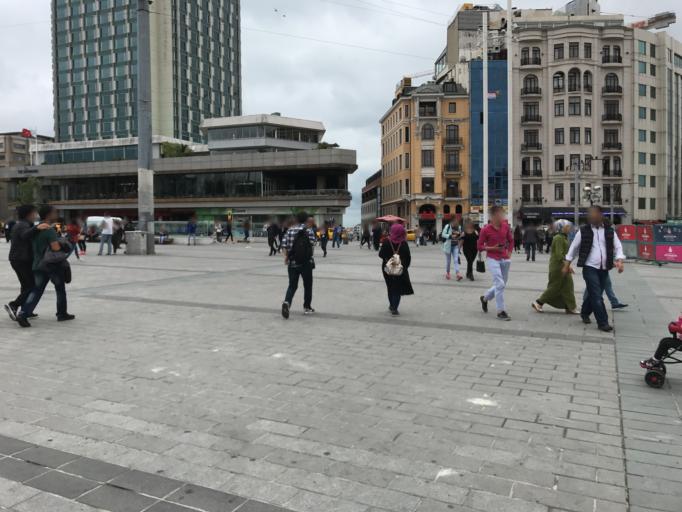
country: TR
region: Istanbul
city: Eminoenue
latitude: 41.0373
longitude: 28.9855
